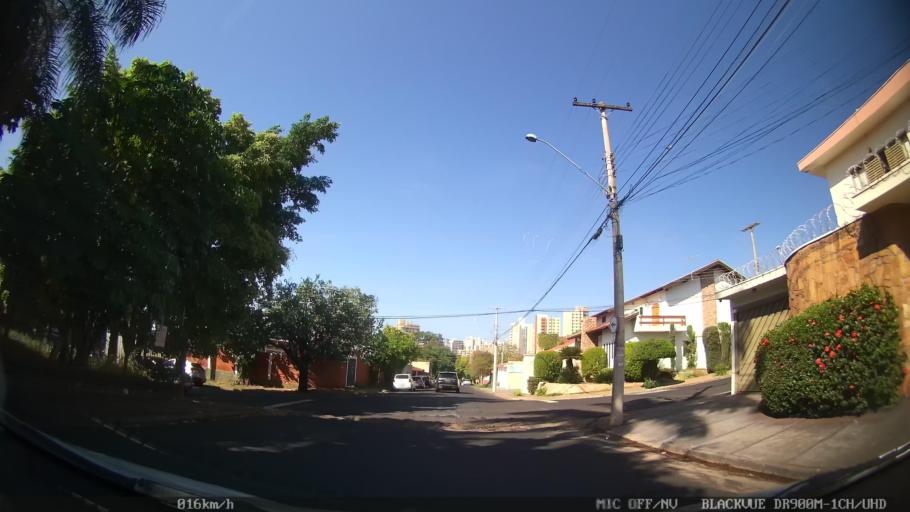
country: BR
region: Sao Paulo
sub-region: Ribeirao Preto
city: Ribeirao Preto
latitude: -21.1963
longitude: -47.8012
